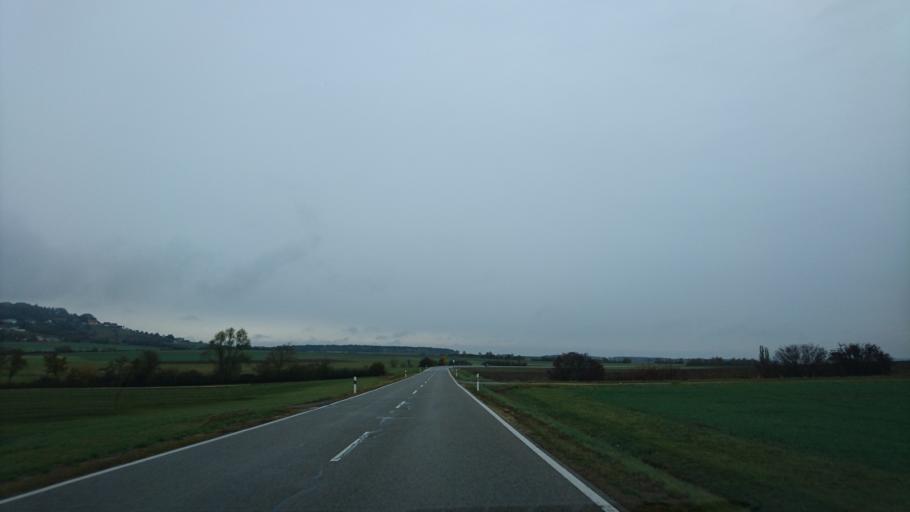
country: DE
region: Bavaria
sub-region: Regierungsbezirk Mittelfranken
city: Bergen
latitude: 49.0951
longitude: 11.1071
